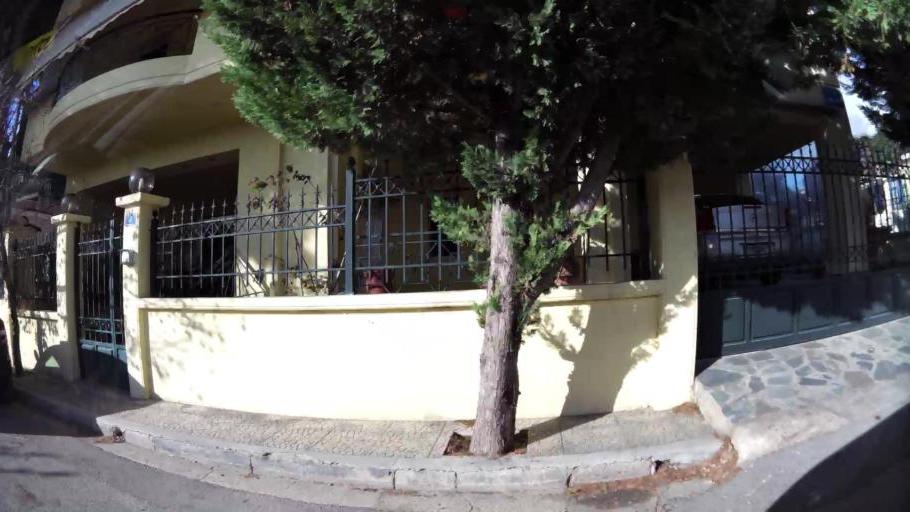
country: GR
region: Attica
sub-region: Nomarchia Anatolikis Attikis
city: Acharnes
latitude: 38.0716
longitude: 23.7460
